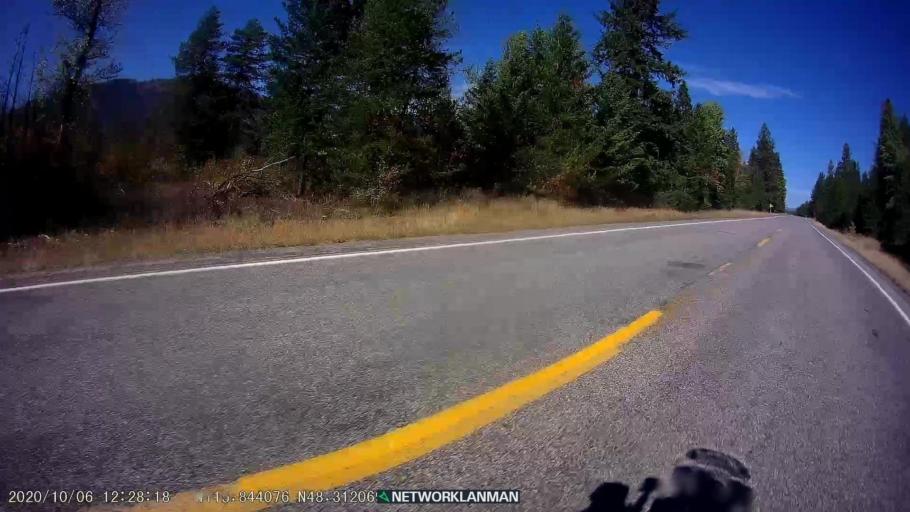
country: US
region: Montana
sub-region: Lincoln County
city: Libby
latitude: 48.3121
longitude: -115.8446
